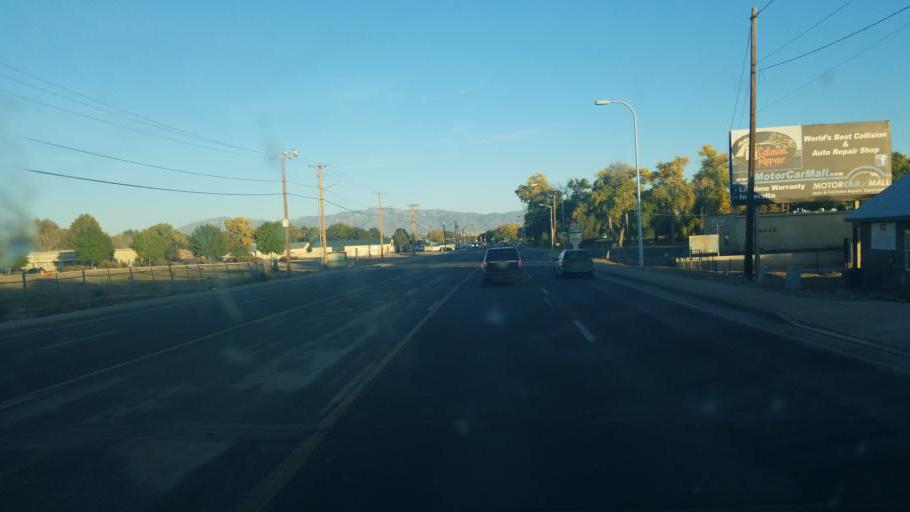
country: US
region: New Mexico
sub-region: Valencia County
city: Valencia
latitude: 34.8036
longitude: -106.7146
